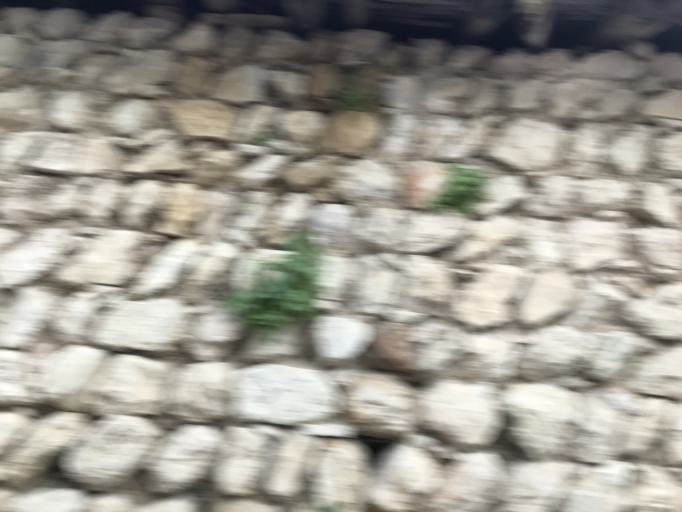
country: TR
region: Hatay
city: Buyukcat
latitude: 36.1014
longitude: 36.0544
